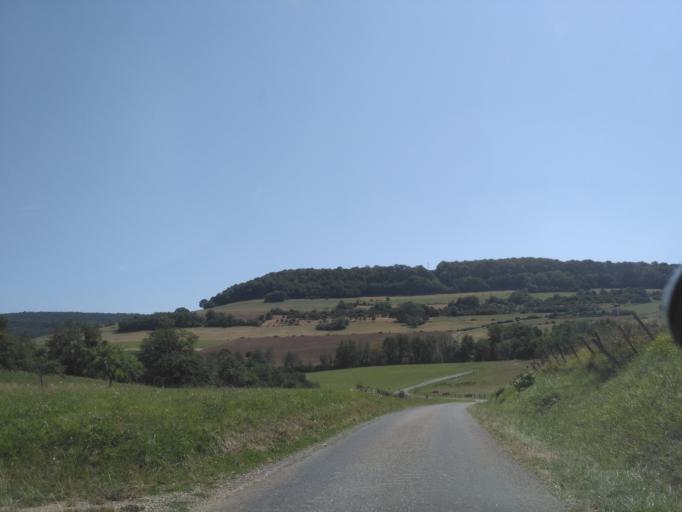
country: FR
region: Franche-Comte
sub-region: Departement de la Haute-Saone
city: Villersexel
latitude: 47.5086
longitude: 6.5177
